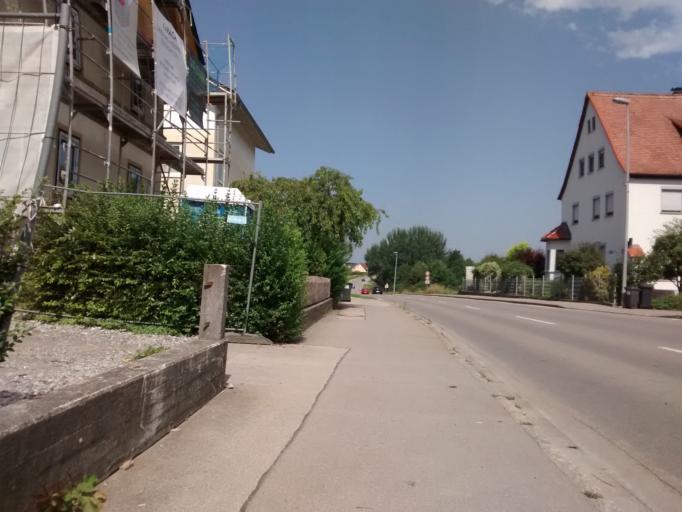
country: DE
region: Baden-Wuerttemberg
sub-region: Tuebingen Region
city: Friedrichshafen
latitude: 47.6703
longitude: 9.4491
